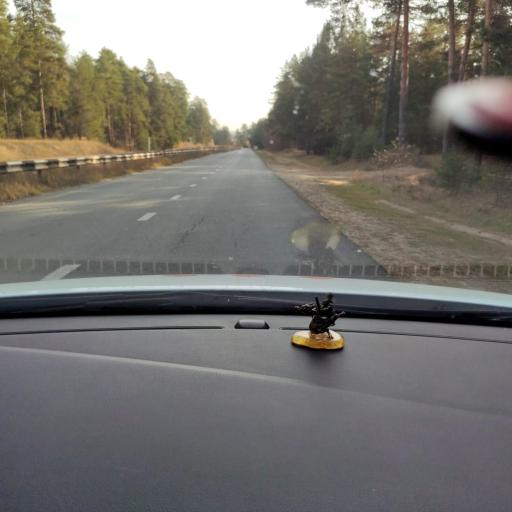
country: RU
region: Tatarstan
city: Osinovo
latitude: 55.8251
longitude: 48.9064
